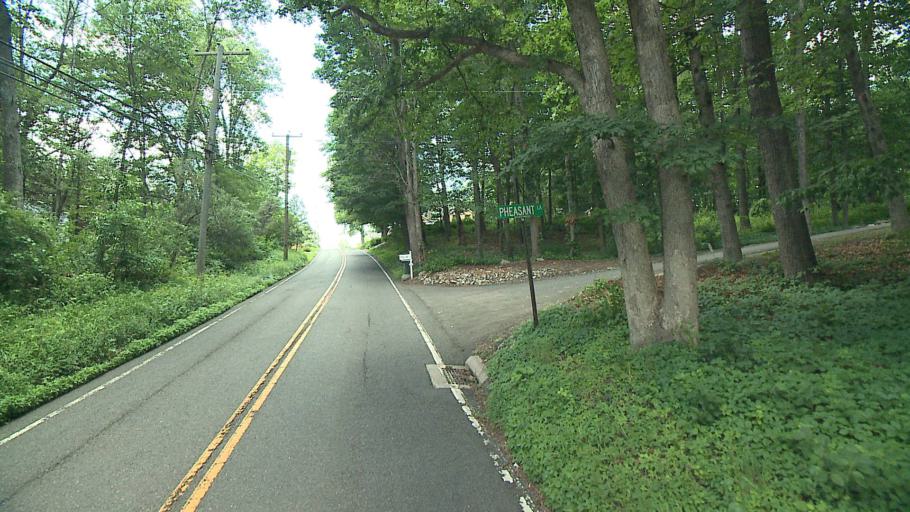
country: US
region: Connecticut
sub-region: Litchfield County
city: New Milford
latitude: 41.5369
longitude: -73.3586
